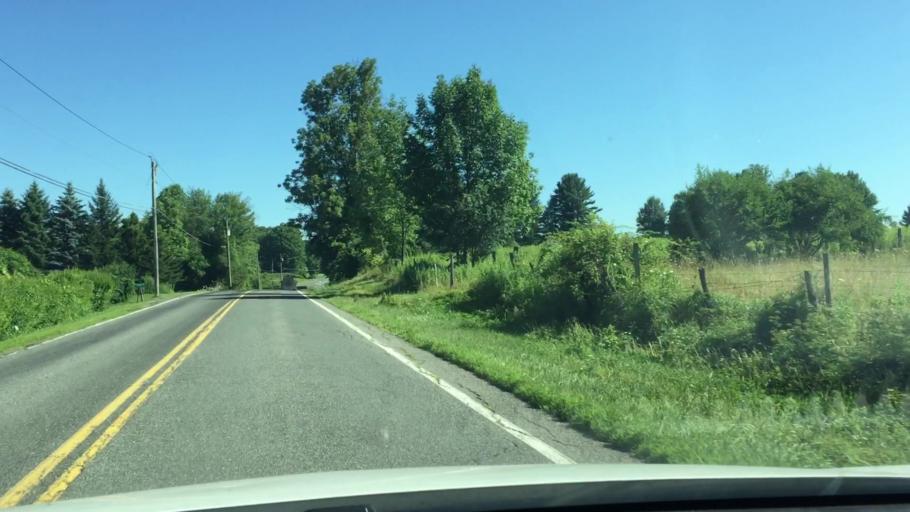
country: US
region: Massachusetts
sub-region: Berkshire County
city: Richmond
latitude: 42.3756
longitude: -73.3456
